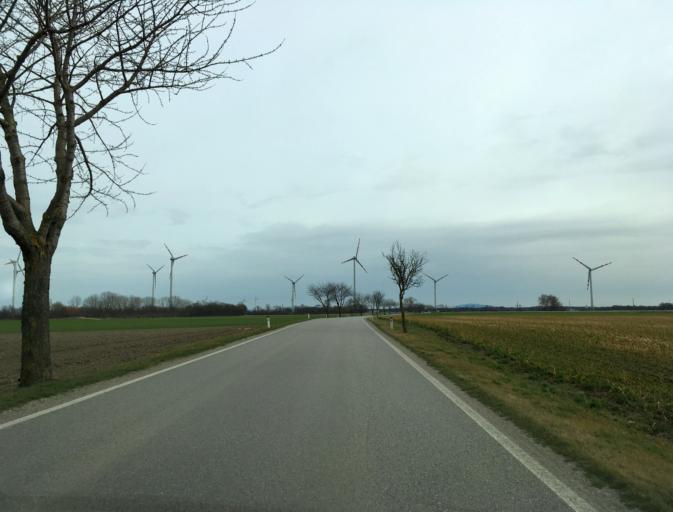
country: AT
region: Lower Austria
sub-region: Politischer Bezirk Ganserndorf
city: Glinzendorf
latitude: 48.2462
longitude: 16.6532
